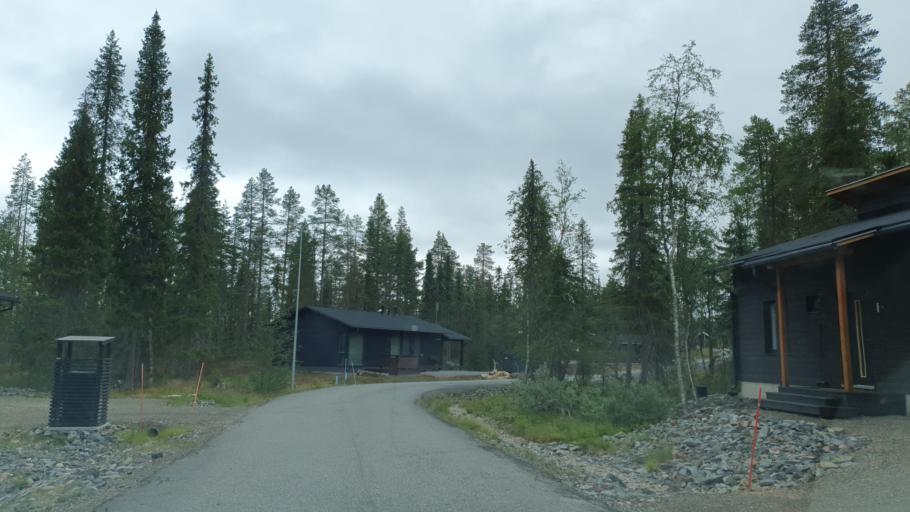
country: FI
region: Lapland
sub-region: Tunturi-Lappi
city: Kolari
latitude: 67.5919
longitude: 24.1739
